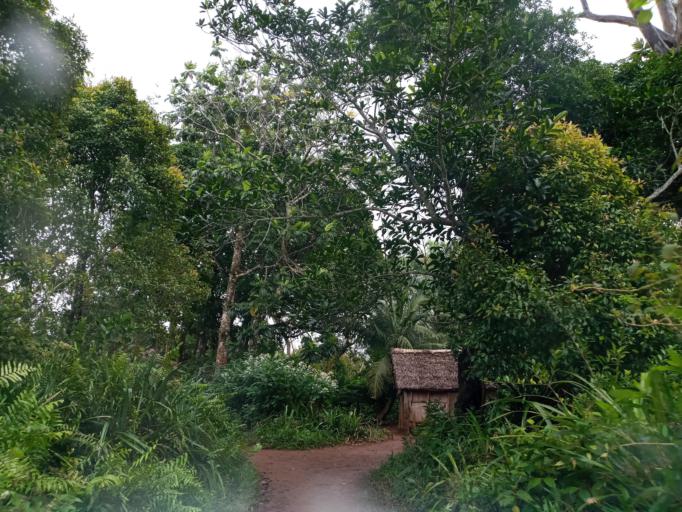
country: MG
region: Atsimo-Atsinanana
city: Vohipaho
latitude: -23.8271
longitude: 47.5449
